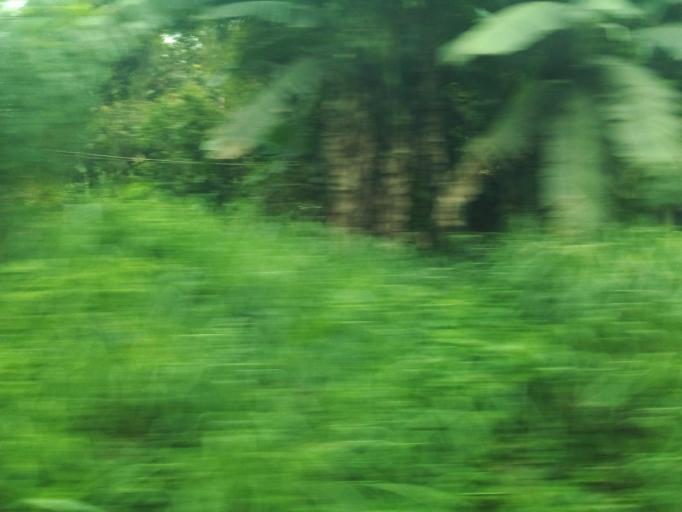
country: BR
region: Minas Gerais
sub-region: Rio Piracicaba
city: Rio Piracicaba
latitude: -19.9023
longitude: -43.1467
